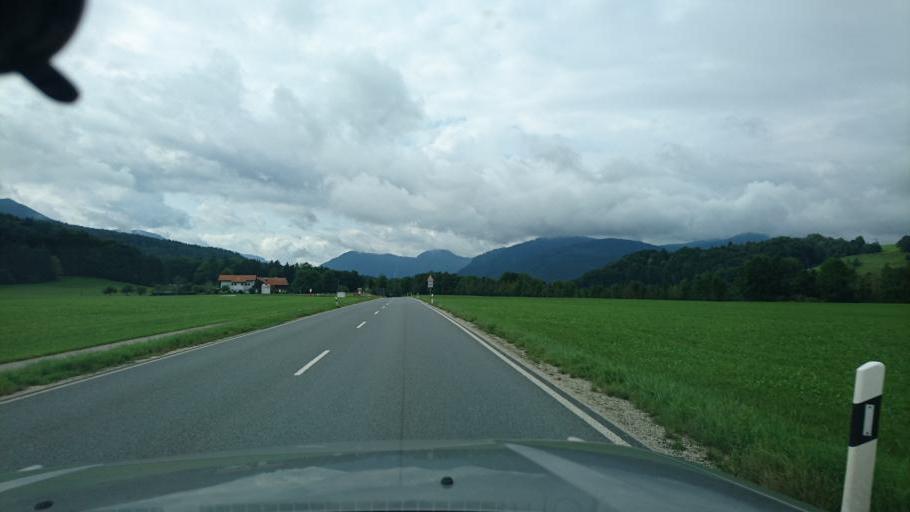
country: DE
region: Bavaria
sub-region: Upper Bavaria
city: Siegsdorf
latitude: 47.8176
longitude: 12.6546
